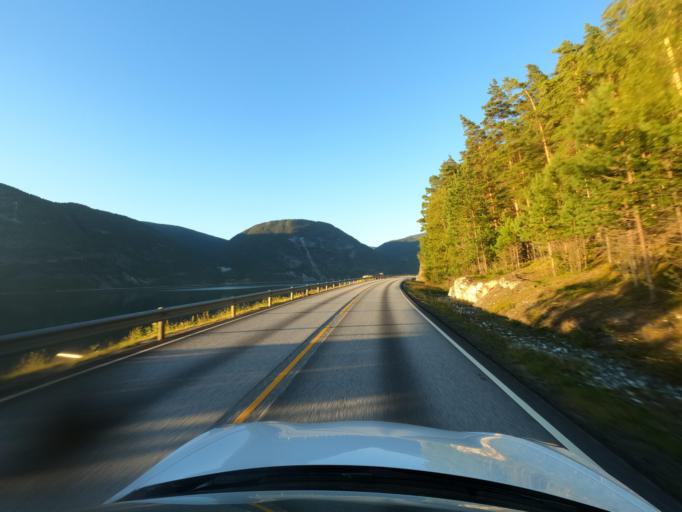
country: NO
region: Sogn og Fjordane
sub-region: Laerdal
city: Laerdalsoyri
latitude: 61.1839
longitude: 7.4896
